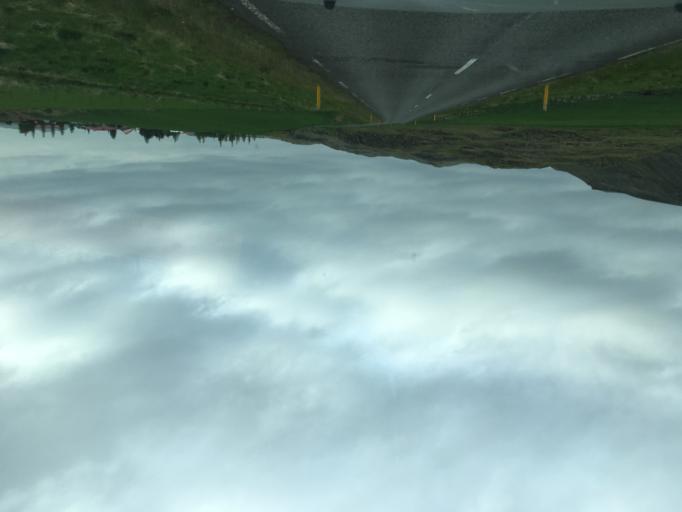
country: IS
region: South
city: Vestmannaeyjar
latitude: 64.1922
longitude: -20.2778
